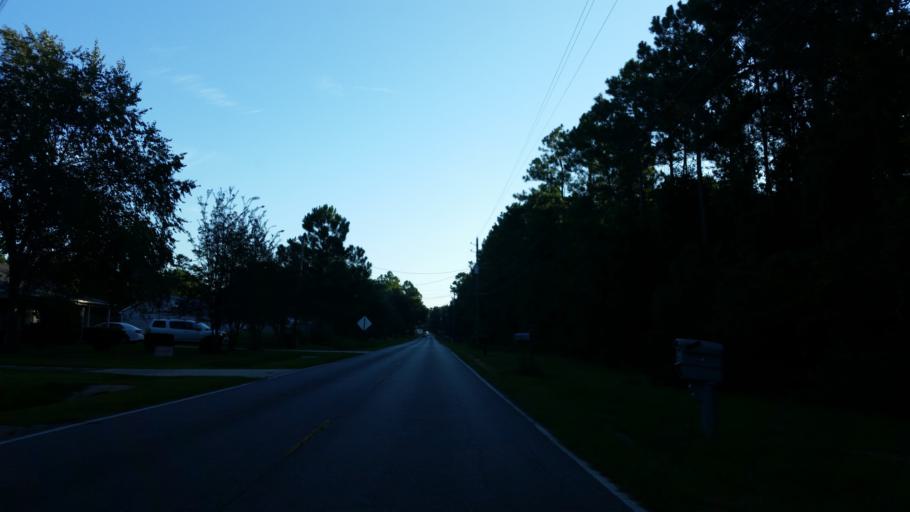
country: US
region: Florida
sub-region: Escambia County
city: Bellview
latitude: 30.4947
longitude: -87.3249
